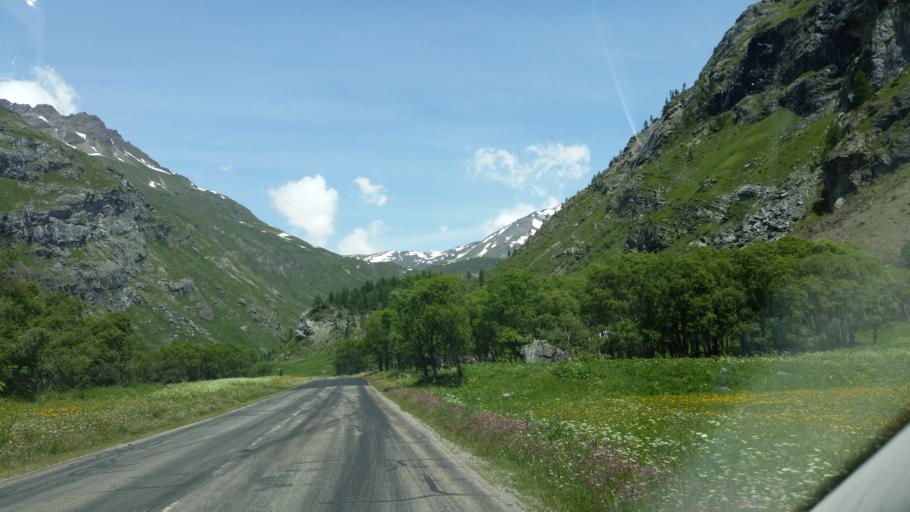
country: FR
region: Rhone-Alpes
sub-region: Departement de la Savoie
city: Val-d'Isere
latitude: 45.3497
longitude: 7.0299
